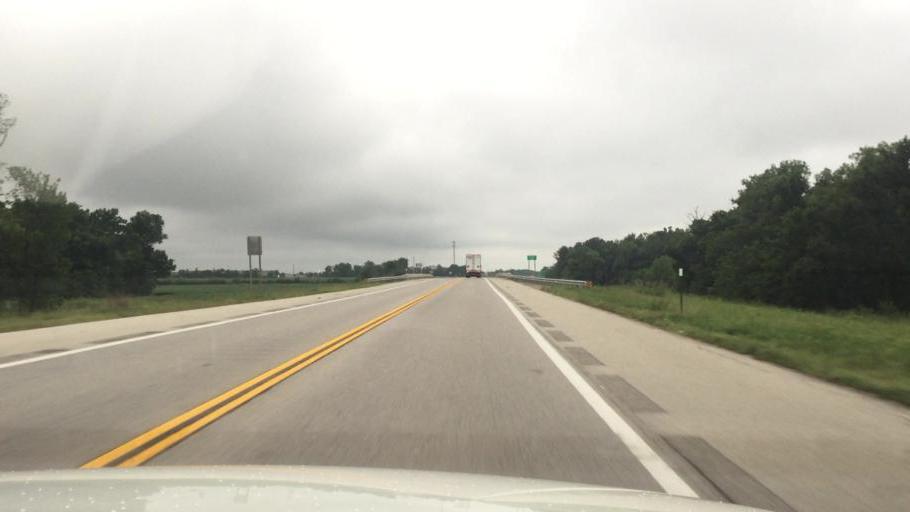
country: US
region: Kansas
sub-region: Montgomery County
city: Coffeyville
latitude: 37.1159
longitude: -95.5837
